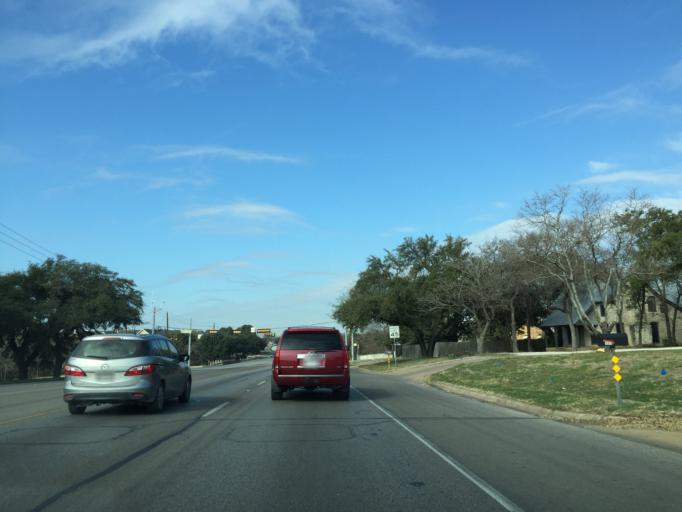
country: US
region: Texas
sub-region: Williamson County
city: Round Rock
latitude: 30.5186
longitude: -97.6721
